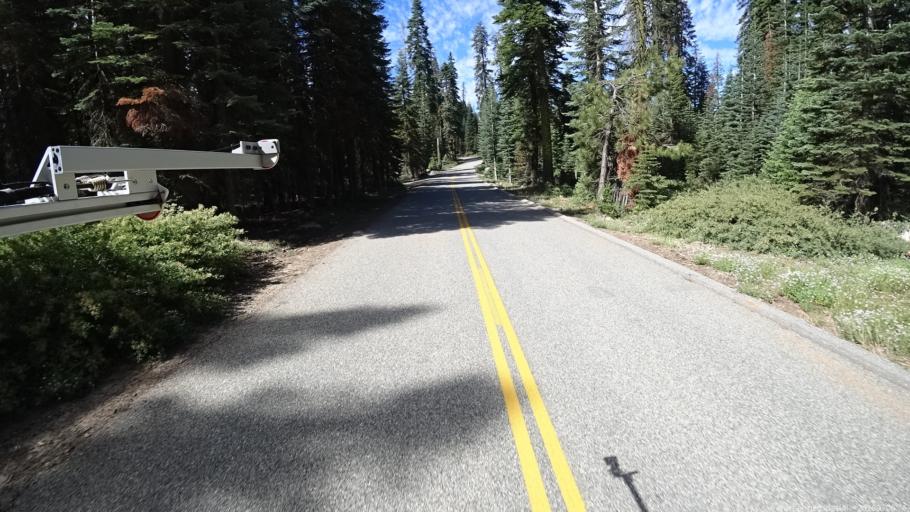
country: US
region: California
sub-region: Madera County
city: Oakhurst
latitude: 37.4037
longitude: -119.5049
